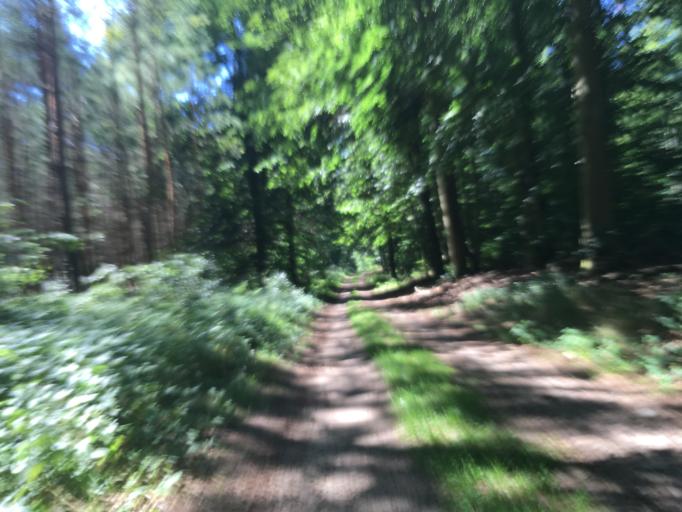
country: DE
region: Brandenburg
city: Grosswoltersdorf
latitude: 53.1271
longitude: 13.0118
